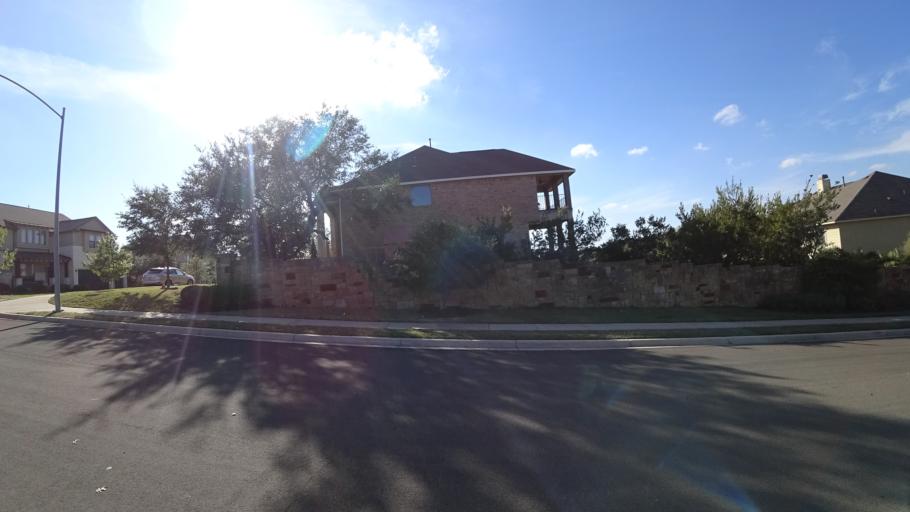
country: US
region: Texas
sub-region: Travis County
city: Barton Creek
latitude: 30.2503
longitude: -97.8778
